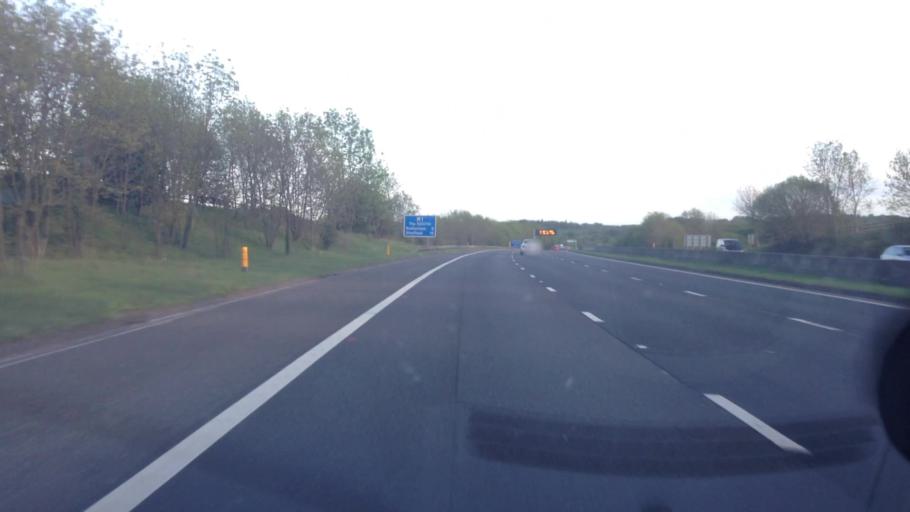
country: GB
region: England
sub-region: Barnsley
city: Hoyland Nether
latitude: 53.4913
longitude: -1.4701
